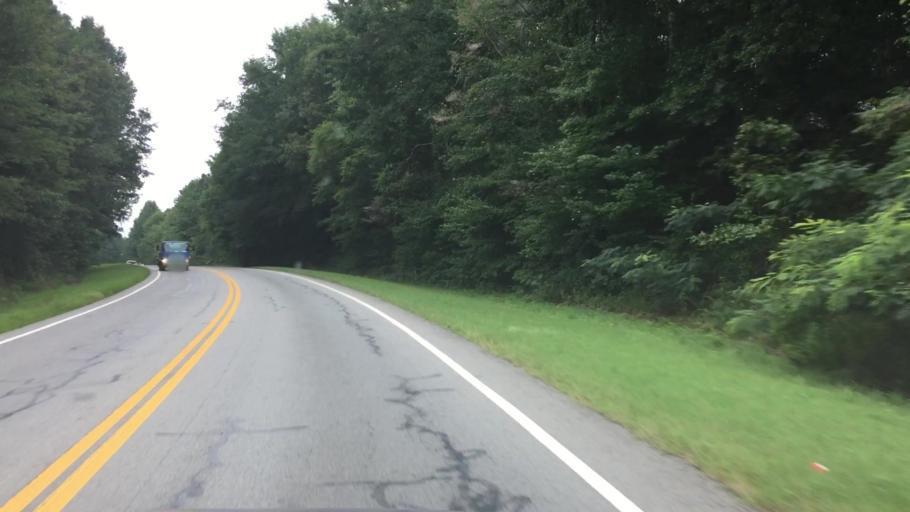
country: US
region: Georgia
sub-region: Jackson County
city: Hoschton
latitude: 34.0600
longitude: -83.7830
